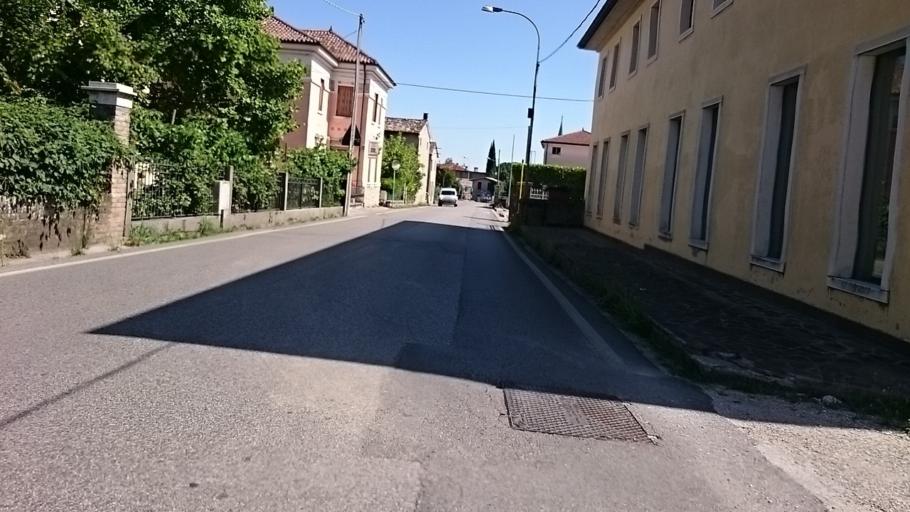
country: IT
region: Veneto
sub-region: Provincia di Treviso
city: Col San Martino
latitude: 45.8989
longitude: 12.0839
